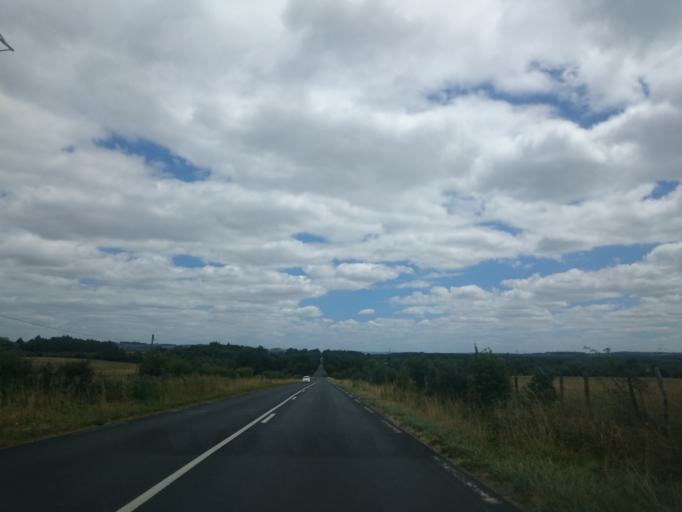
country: FR
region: Auvergne
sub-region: Departement du Cantal
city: Saint-Paul-des-Landes
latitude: 44.9601
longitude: 2.2644
